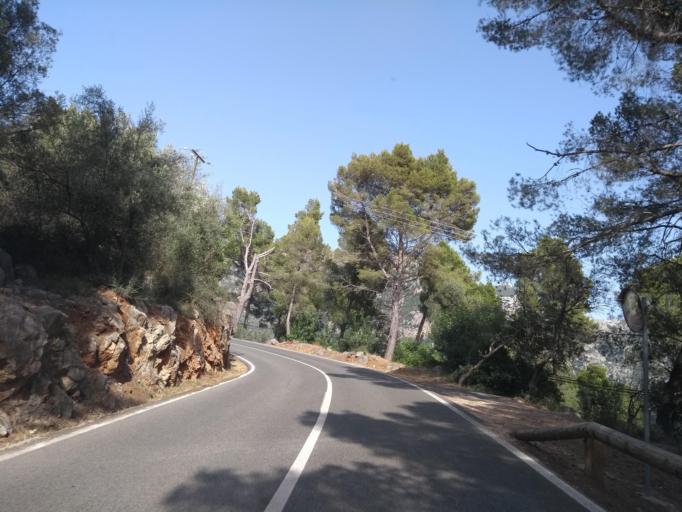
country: ES
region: Balearic Islands
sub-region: Illes Balears
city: Soller
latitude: 39.7788
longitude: 2.7218
